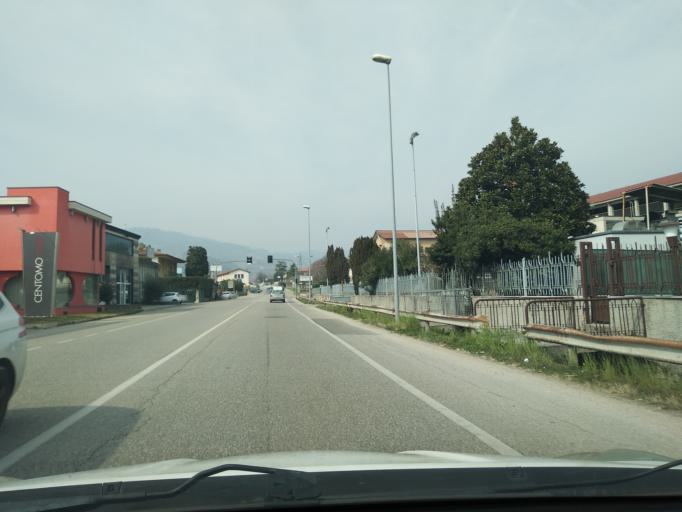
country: IT
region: Veneto
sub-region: Provincia di Vicenza
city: Chiampo
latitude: 45.5361
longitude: 11.2977
